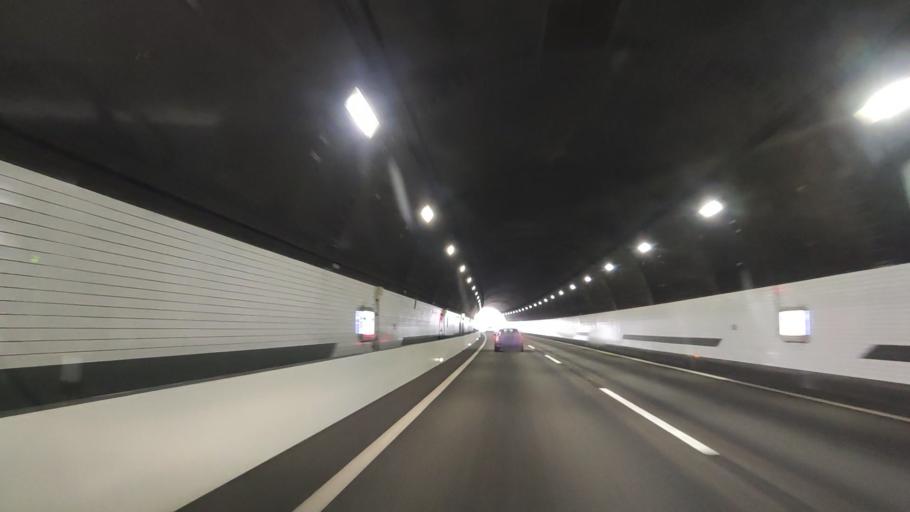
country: JP
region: Tokushima
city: Ishii
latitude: 34.1963
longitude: 134.4323
